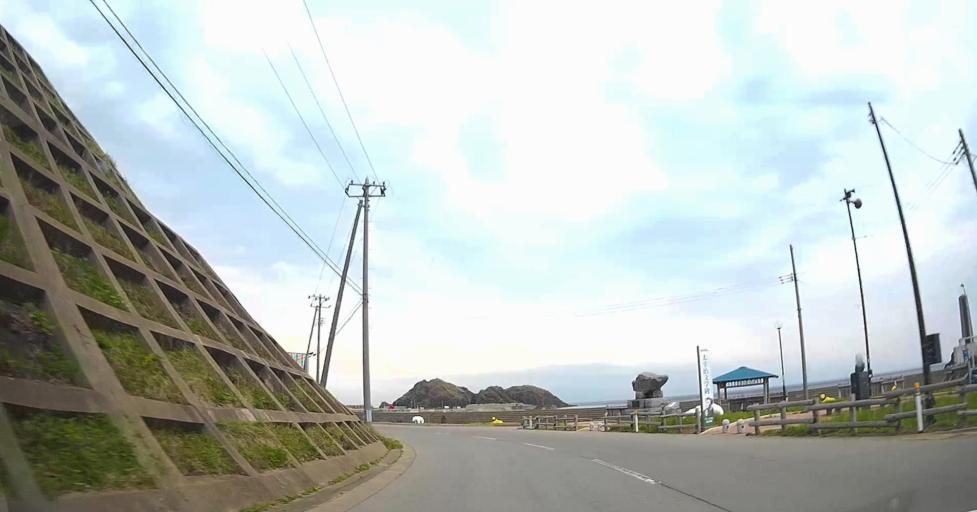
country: JP
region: Aomori
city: Shimokizukuri
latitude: 41.2579
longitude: 140.3490
